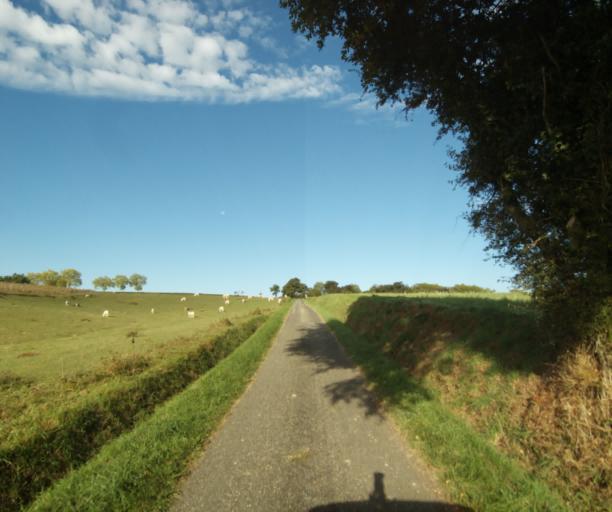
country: FR
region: Midi-Pyrenees
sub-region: Departement du Gers
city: Eauze
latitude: 43.8939
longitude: 0.0351
